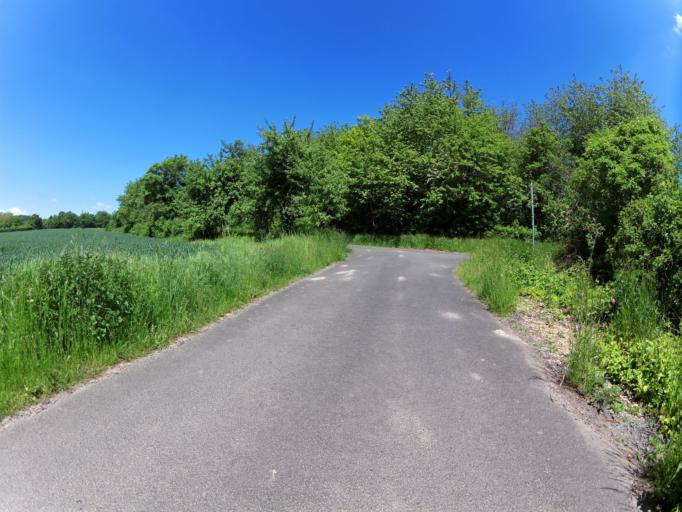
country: DE
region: Thuringia
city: Dankmarshausen
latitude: 50.9544
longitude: 10.0008
